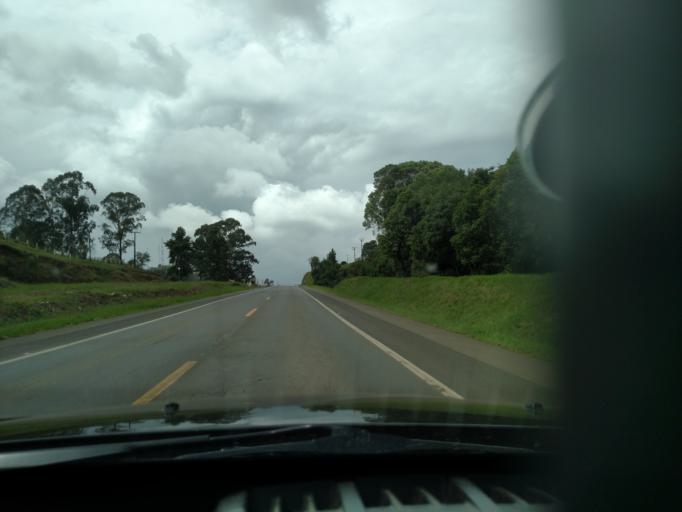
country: BR
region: Santa Catarina
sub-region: Lages
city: Lages
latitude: -27.8223
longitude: -50.3764
